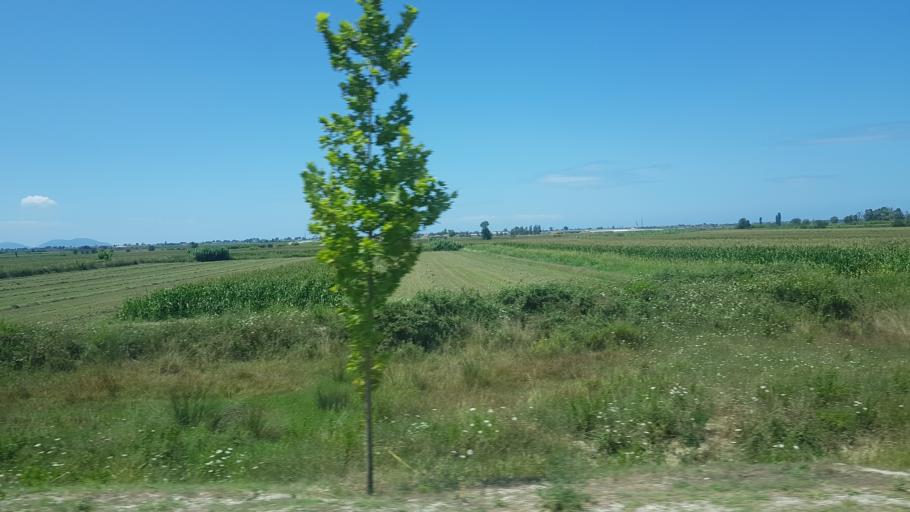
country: AL
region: Fier
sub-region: Rrethi i Fierit
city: Frakulla e Madhe
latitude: 40.6600
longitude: 19.4896
